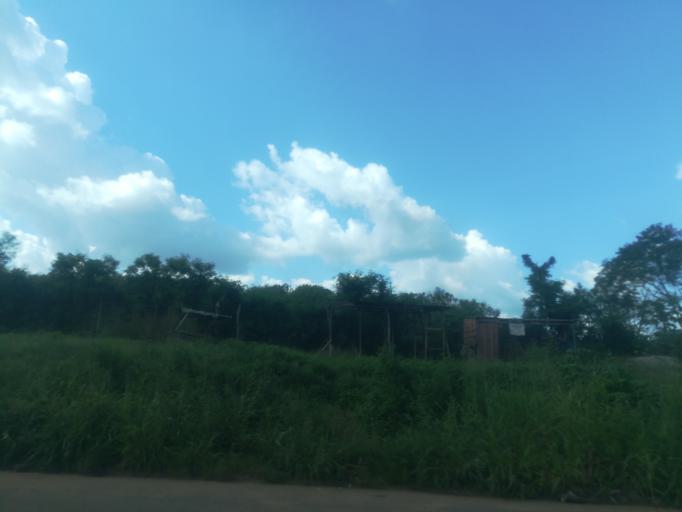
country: NG
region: Oyo
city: Egbeda
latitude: 7.4235
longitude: 3.9833
